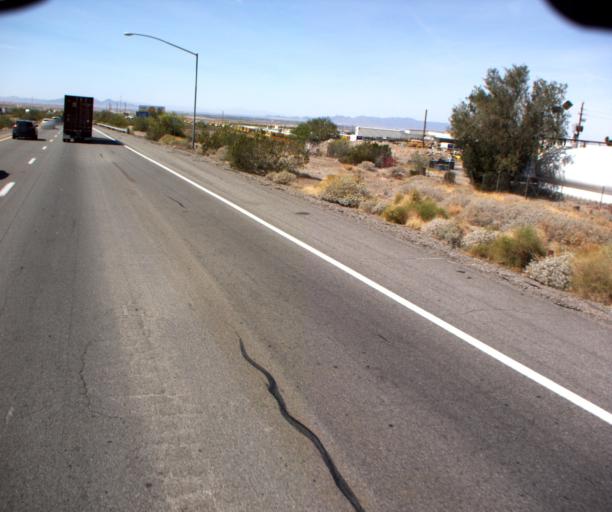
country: US
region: Arizona
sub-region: La Paz County
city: Ehrenberg
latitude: 33.6235
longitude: -114.4377
